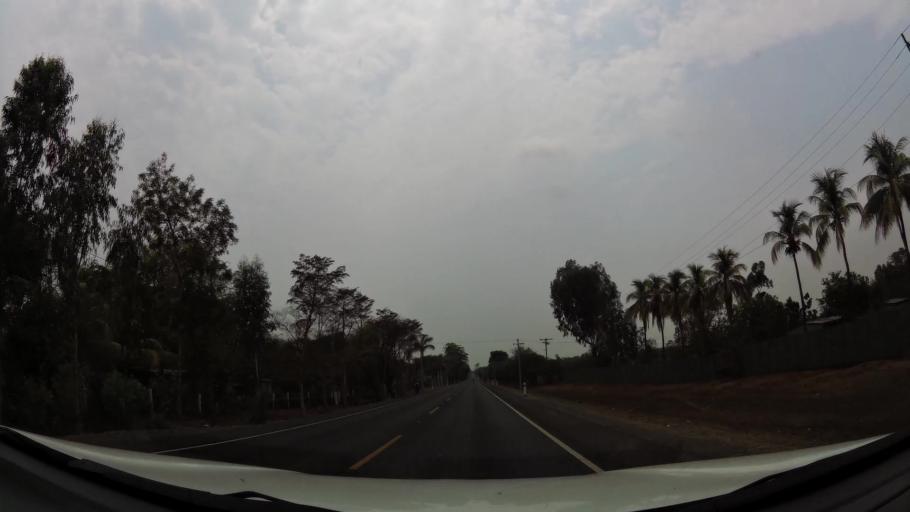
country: NI
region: Chinandega
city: Chichigalpa
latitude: 12.6063
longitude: -87.0620
